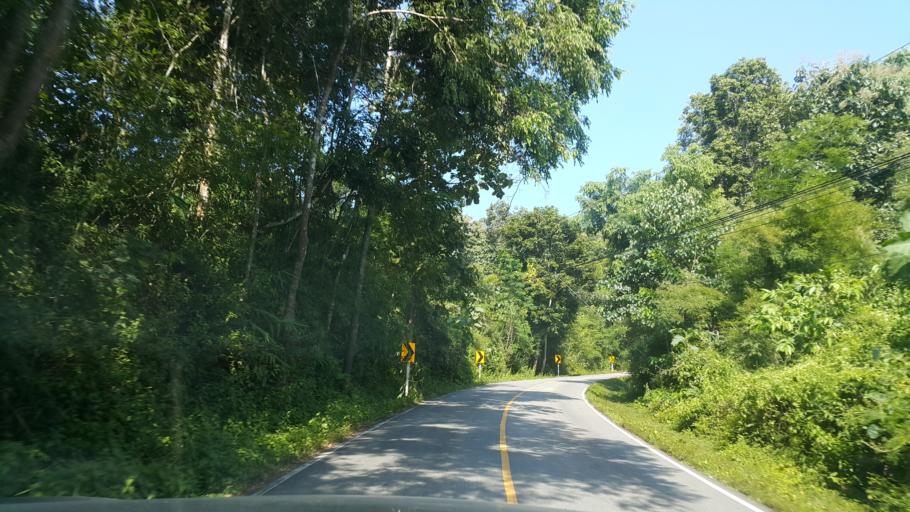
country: TH
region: Chiang Mai
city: Samoeng
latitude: 18.8587
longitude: 98.6541
